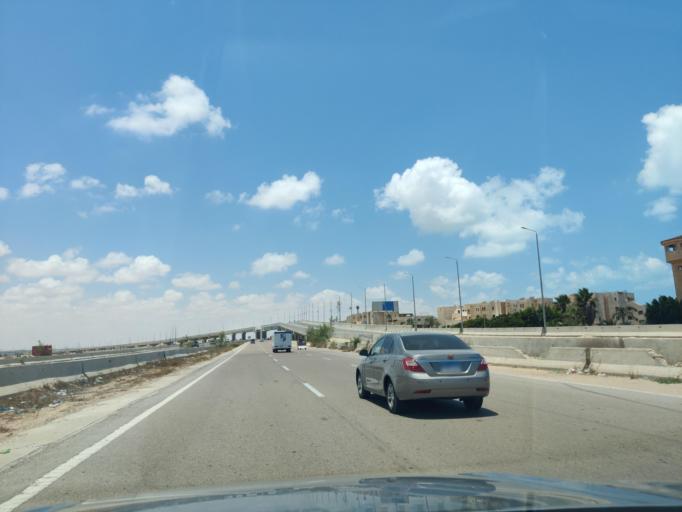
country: EG
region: Muhafazat Matruh
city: Al `Alamayn
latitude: 30.8127
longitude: 29.0639
